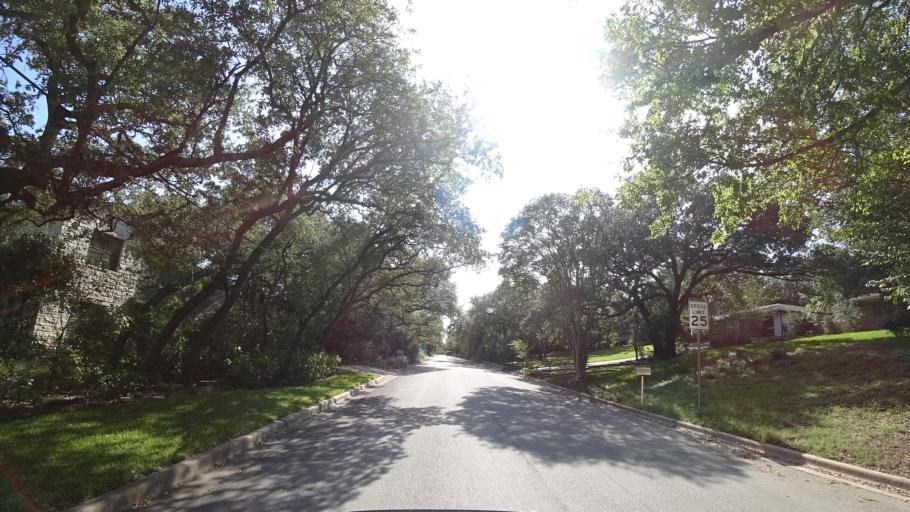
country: US
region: Texas
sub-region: Travis County
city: West Lake Hills
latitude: 30.2859
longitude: -97.8088
